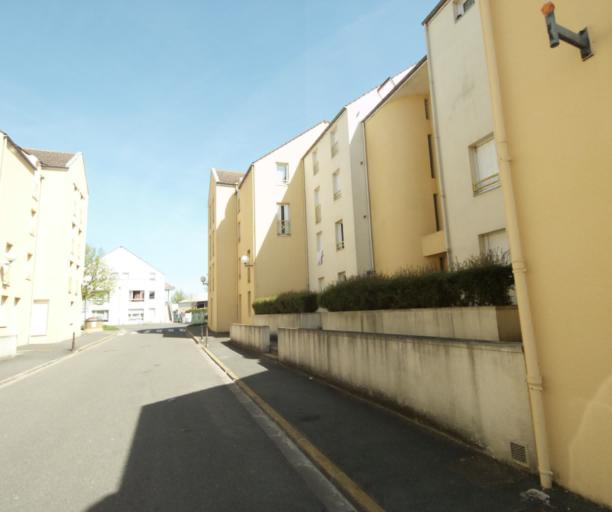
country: FR
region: Ile-de-France
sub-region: Departement de Seine-et-Marne
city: Nangis
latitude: 48.5533
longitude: 3.0060
